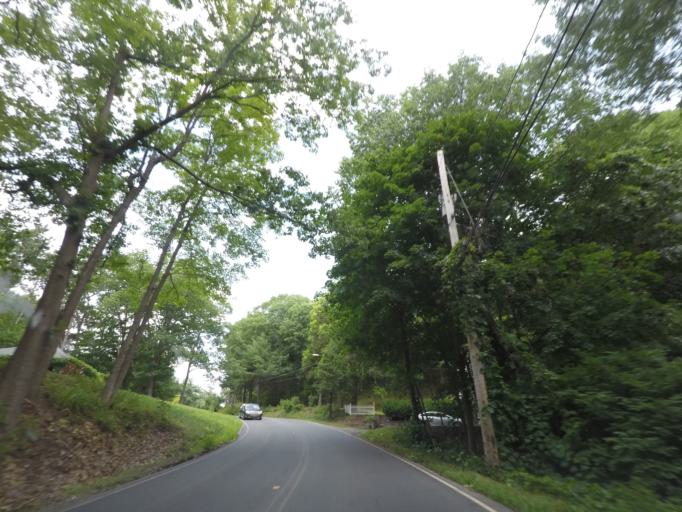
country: US
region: New York
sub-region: Rensselaer County
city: Wynantskill
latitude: 42.6948
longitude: -73.6276
